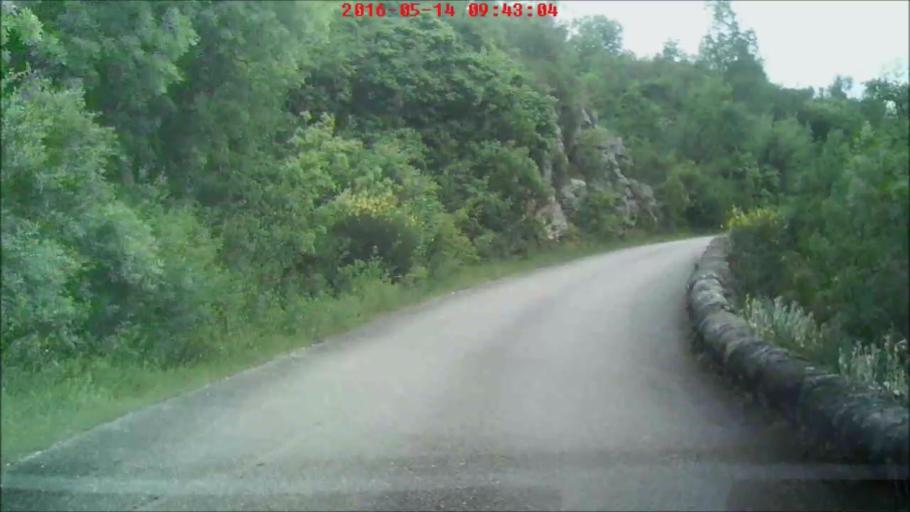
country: HR
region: Dubrovacko-Neretvanska
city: Podgora
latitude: 42.7875
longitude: 17.9046
